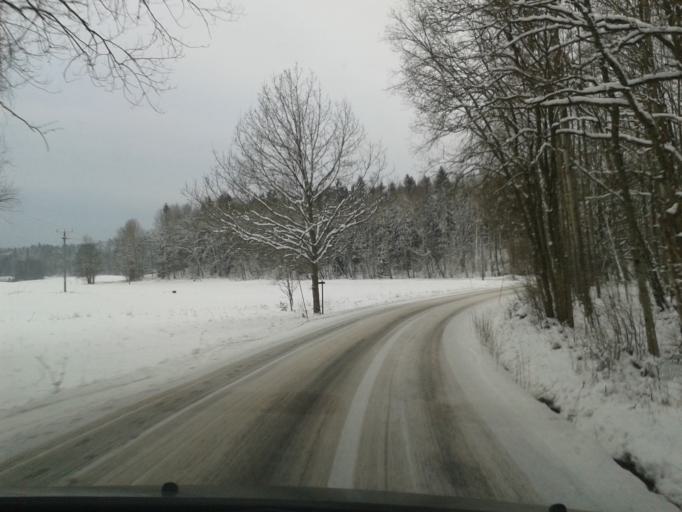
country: SE
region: Stockholm
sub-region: Nacka Kommun
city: Saltsjobaden
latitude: 59.2176
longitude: 18.3062
